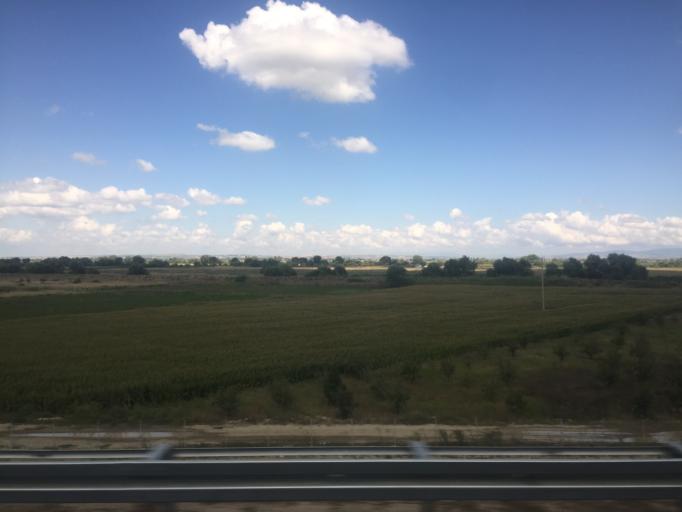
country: TR
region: Bursa
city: Karacabey
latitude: 40.1228
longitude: 28.2825
